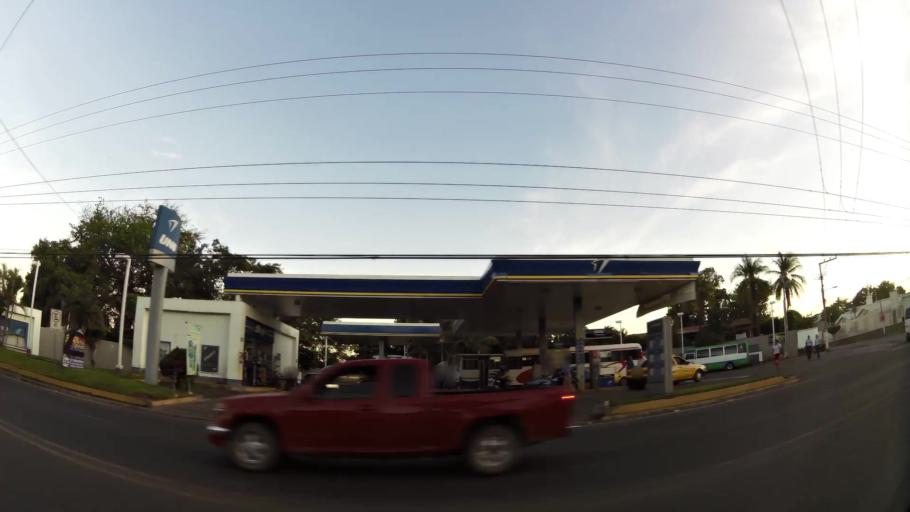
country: SV
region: San Miguel
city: San Miguel
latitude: 13.4938
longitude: -88.1753
